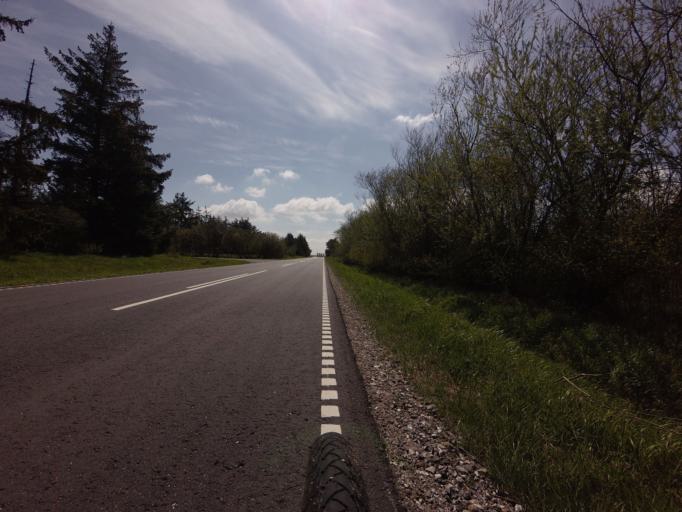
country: DK
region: North Denmark
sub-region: Jammerbugt Kommune
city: Brovst
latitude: 57.1571
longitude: 9.5762
